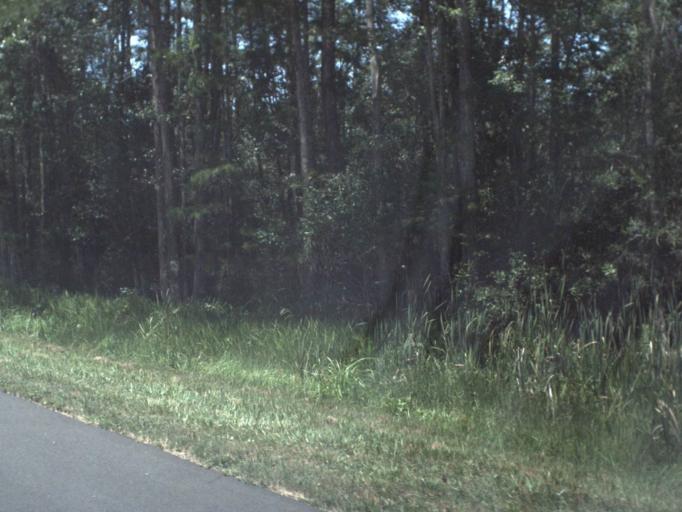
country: US
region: Florida
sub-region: Union County
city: Lake Butler
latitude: 30.0285
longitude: -82.3196
